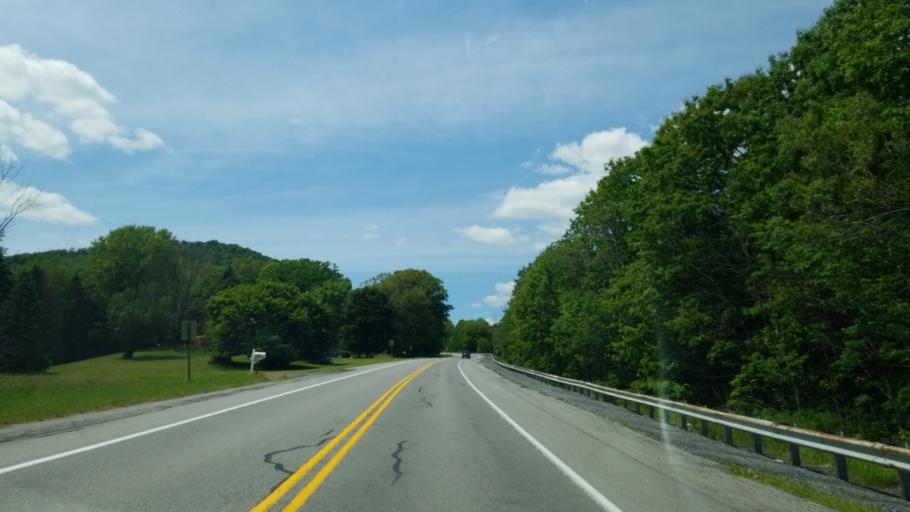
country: US
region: Pennsylvania
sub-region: Blair County
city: Tyrone
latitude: 40.6905
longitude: -78.2742
